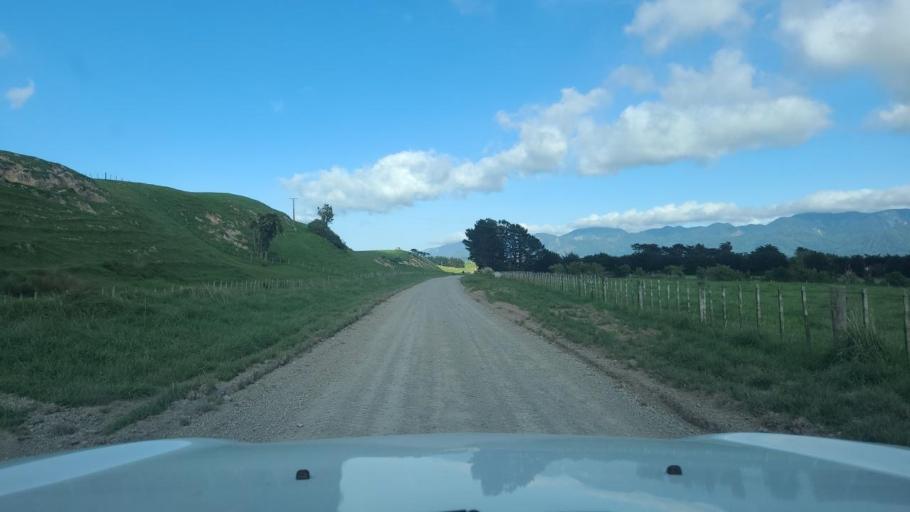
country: NZ
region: Wellington
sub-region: Upper Hutt City
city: Upper Hutt
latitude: -41.3384
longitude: 175.1997
